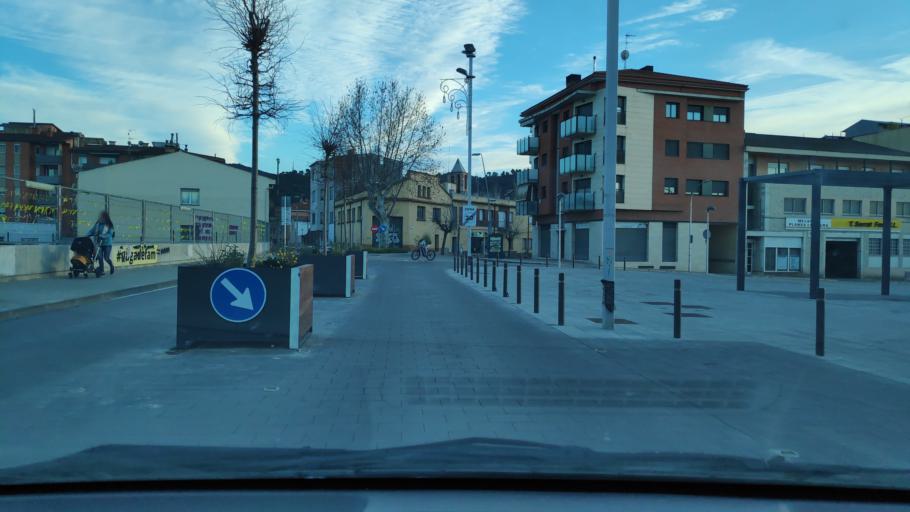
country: ES
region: Catalonia
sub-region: Provincia de Barcelona
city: Montmelo
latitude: 41.5510
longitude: 2.2486
